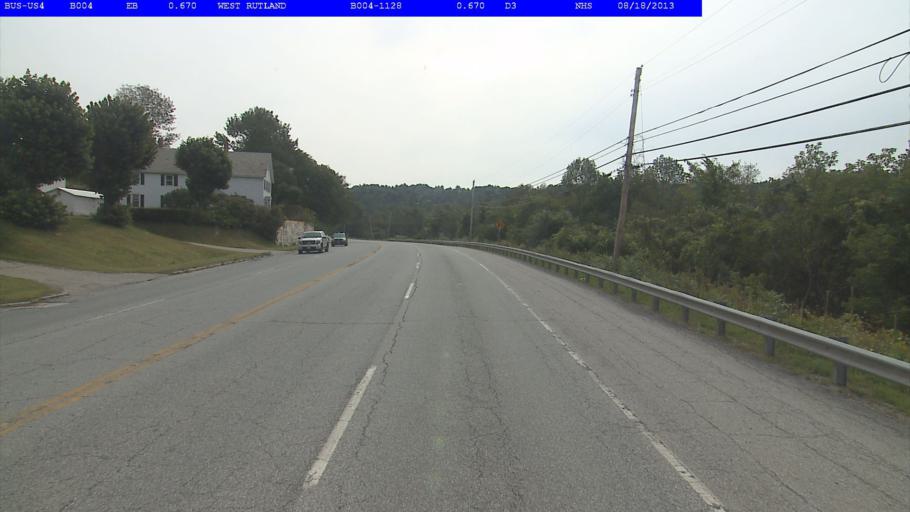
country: US
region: Vermont
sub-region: Rutland County
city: West Rutland
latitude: 43.5937
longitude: -73.0364
